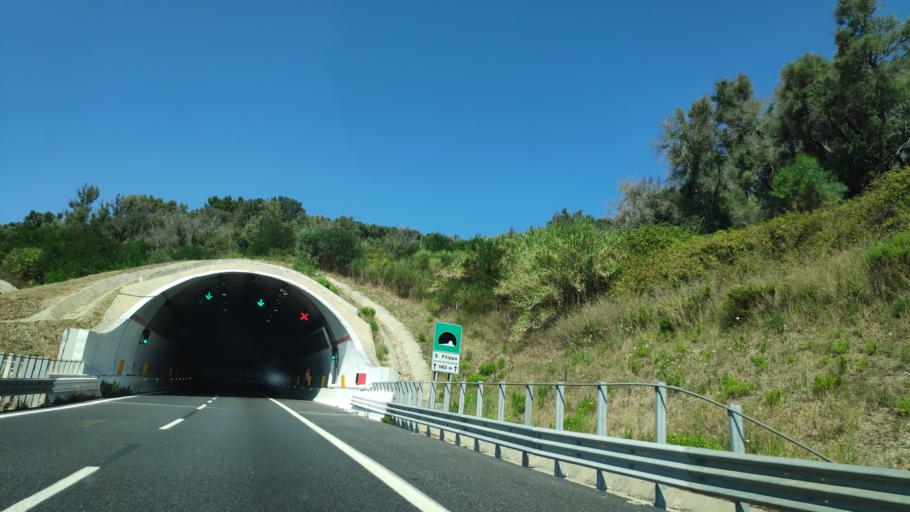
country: IT
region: Calabria
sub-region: Provincia di Reggio Calabria
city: Palmi
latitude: 38.3826
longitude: 15.8820
